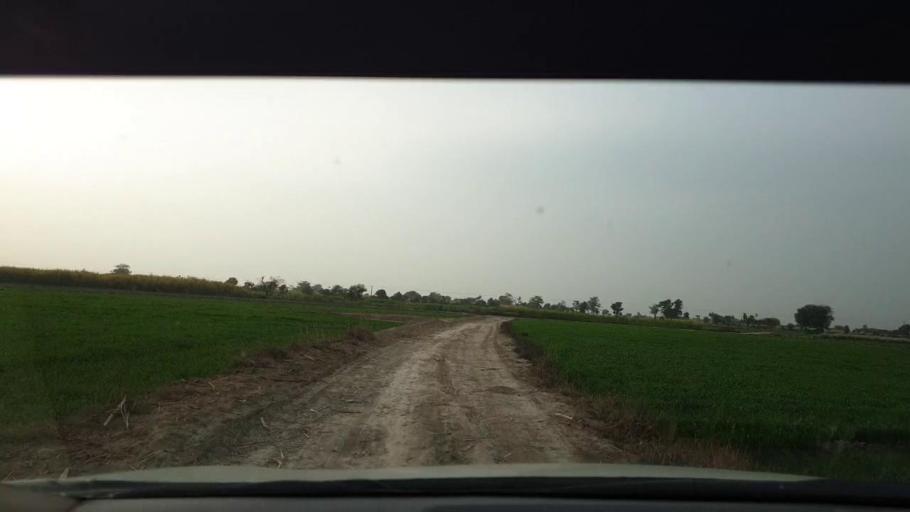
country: PK
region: Sindh
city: Jhol
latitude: 25.9096
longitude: 68.7842
